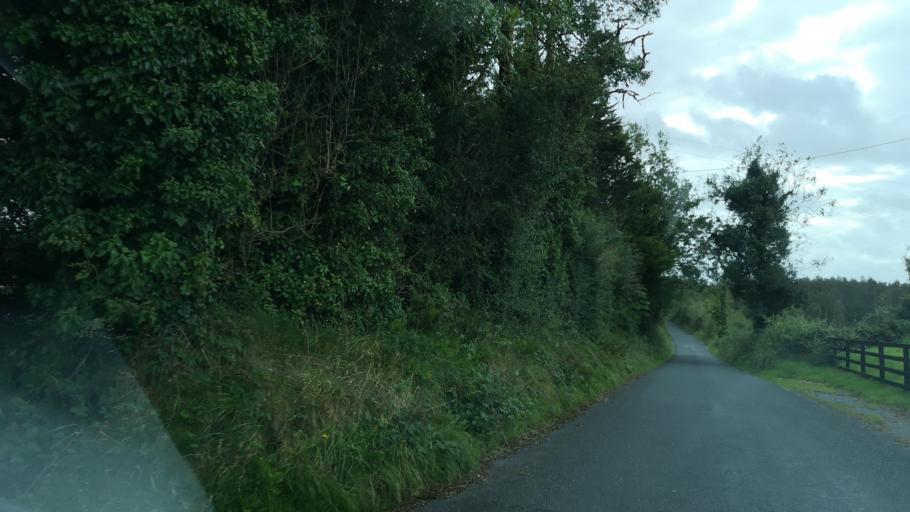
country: IE
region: Connaught
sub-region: County Galway
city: Loughrea
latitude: 53.2924
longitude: -8.5906
